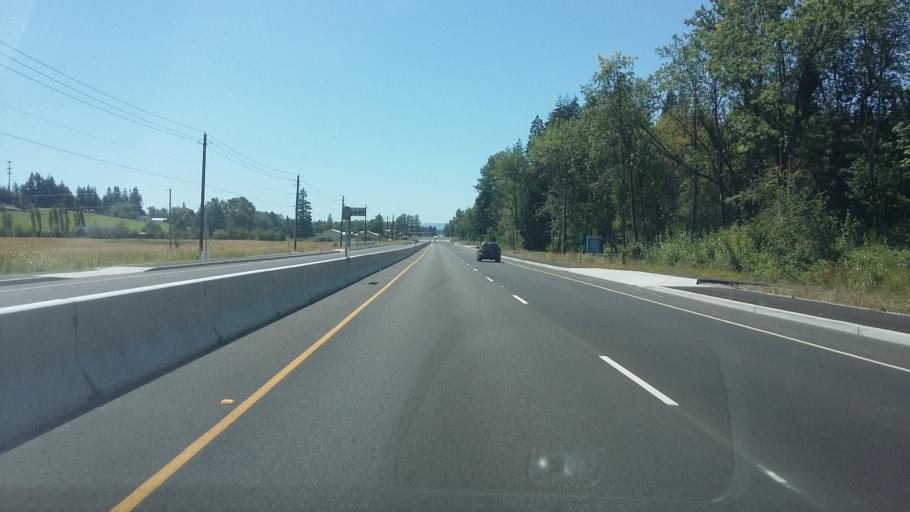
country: US
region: Washington
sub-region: Clark County
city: Meadow Glade
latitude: 45.7805
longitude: -122.5713
